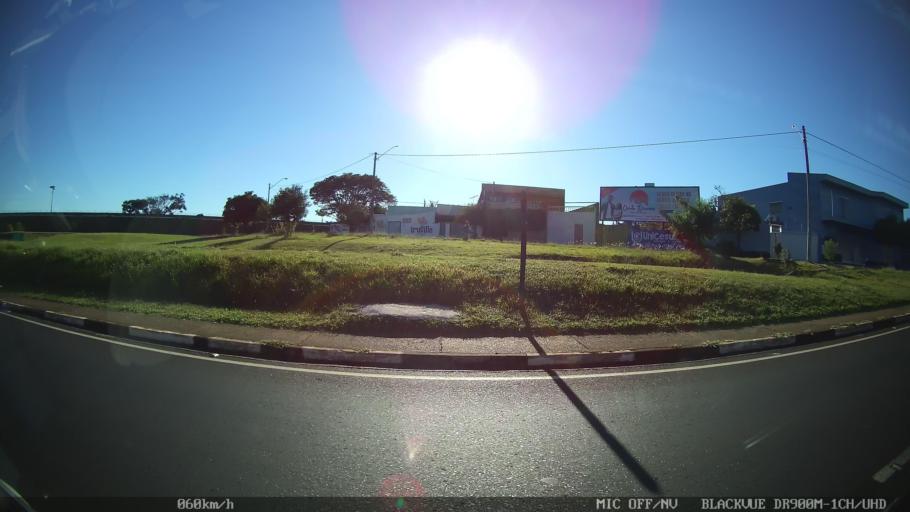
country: BR
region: Sao Paulo
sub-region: Franca
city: Franca
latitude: -20.5718
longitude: -47.3916
